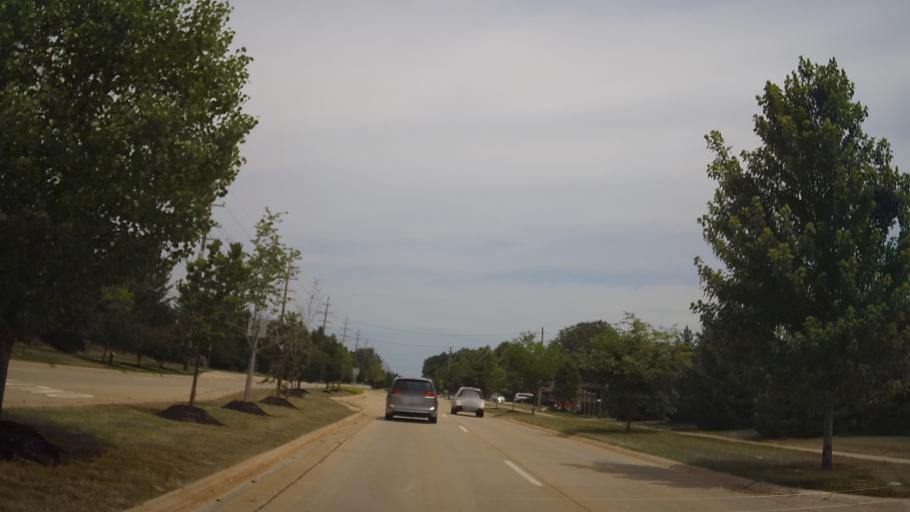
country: US
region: Michigan
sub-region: Macomb County
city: Utica
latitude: 42.6083
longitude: -83.0681
